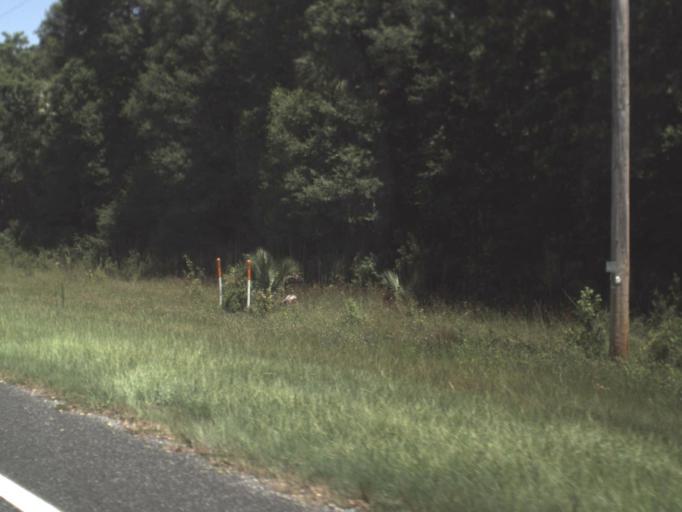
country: US
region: Florida
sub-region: Dixie County
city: Cross City
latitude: 29.6773
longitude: -83.2490
